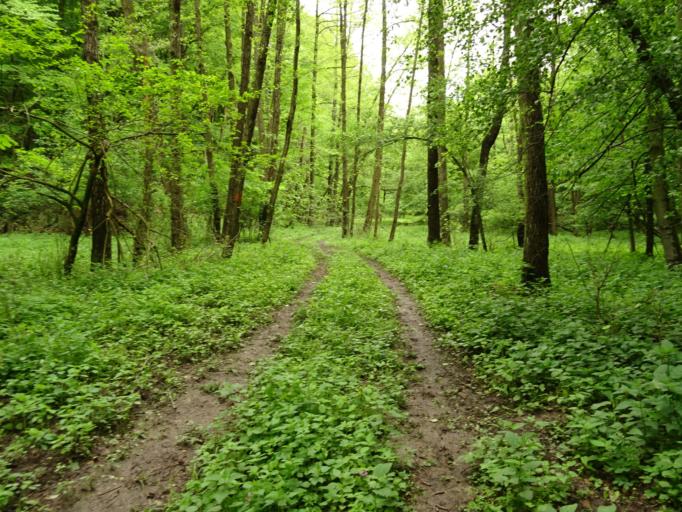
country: HU
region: Veszprem
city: Herend
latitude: 47.1734
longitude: 17.6707
